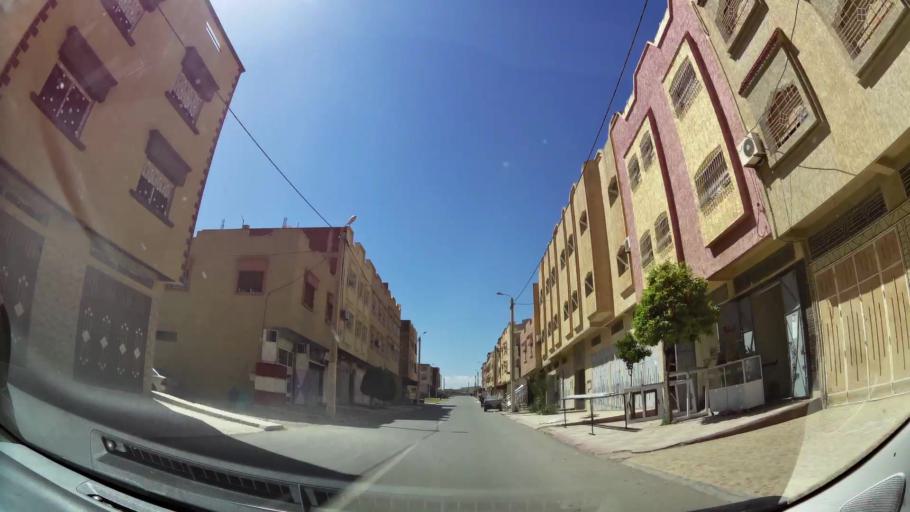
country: MA
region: Oriental
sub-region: Oujda-Angad
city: Oujda
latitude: 34.6648
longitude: -1.8766
